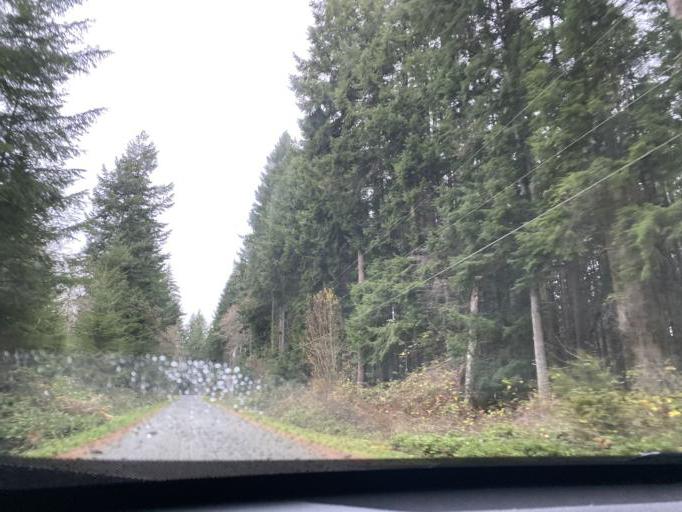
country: US
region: Washington
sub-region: Island County
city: Langley
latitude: 48.0260
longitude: -122.4625
